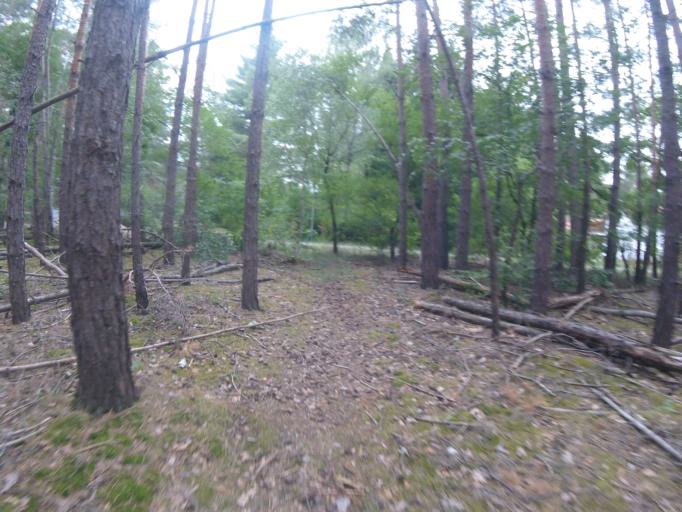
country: DE
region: Brandenburg
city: Bestensee
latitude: 52.2513
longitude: 13.6819
